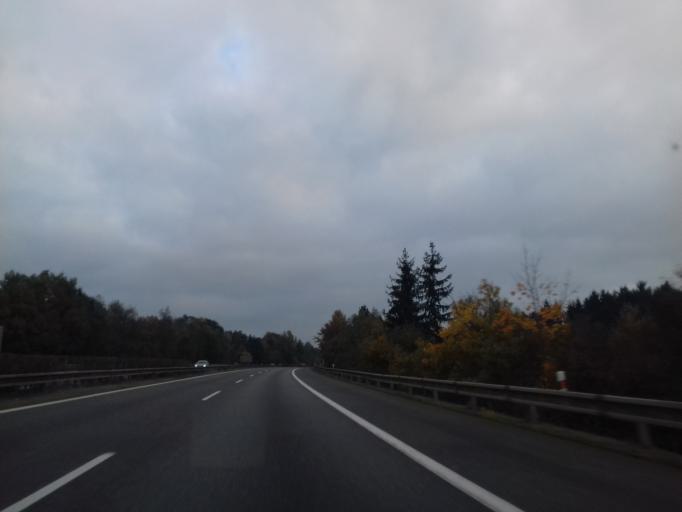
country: CZ
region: Central Bohemia
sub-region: Okres Praha-Vychod
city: Mnichovice
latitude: 49.9076
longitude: 14.7314
